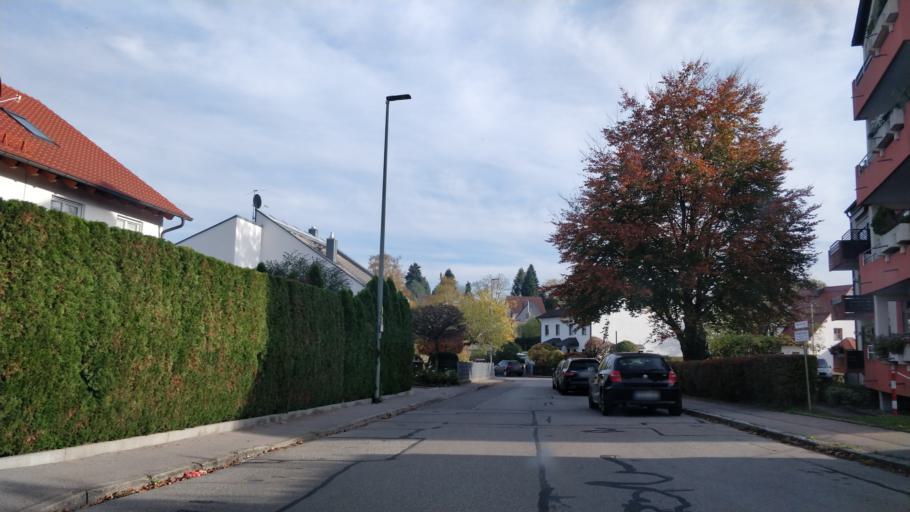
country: DE
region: Bavaria
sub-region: Swabia
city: Stadtbergen
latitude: 48.3731
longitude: 10.8219
